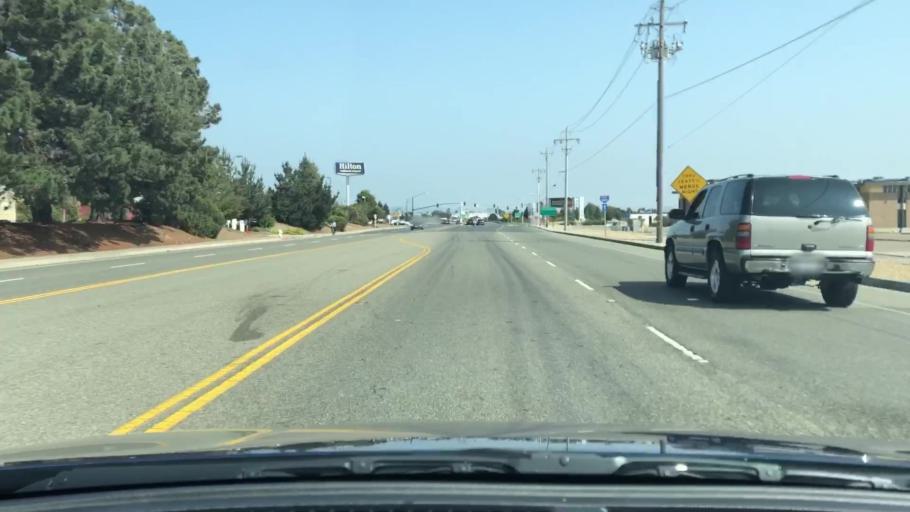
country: US
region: California
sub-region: Alameda County
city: San Leandro
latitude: 37.7280
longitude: -122.2046
